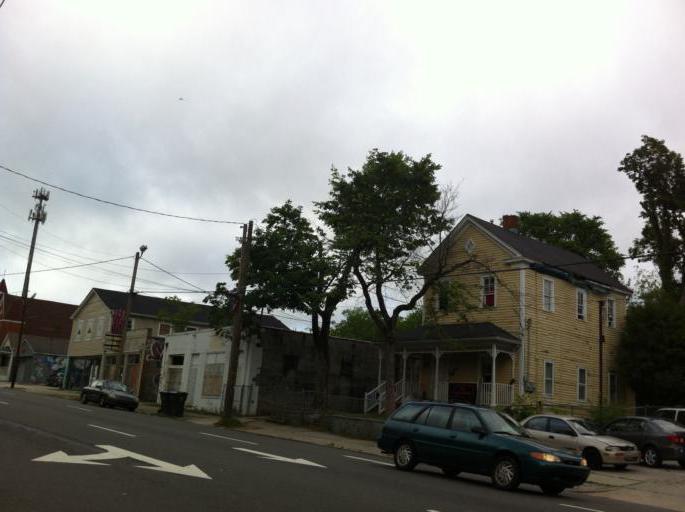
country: US
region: North Carolina
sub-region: Wake County
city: Raleigh
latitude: 35.7730
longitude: -78.6369
